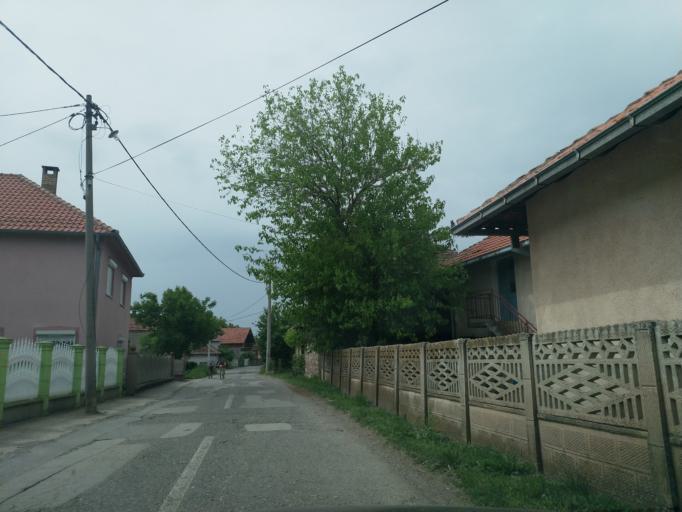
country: RS
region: Central Serbia
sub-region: Pomoravski Okrug
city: Paracin
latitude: 43.8571
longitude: 21.5947
